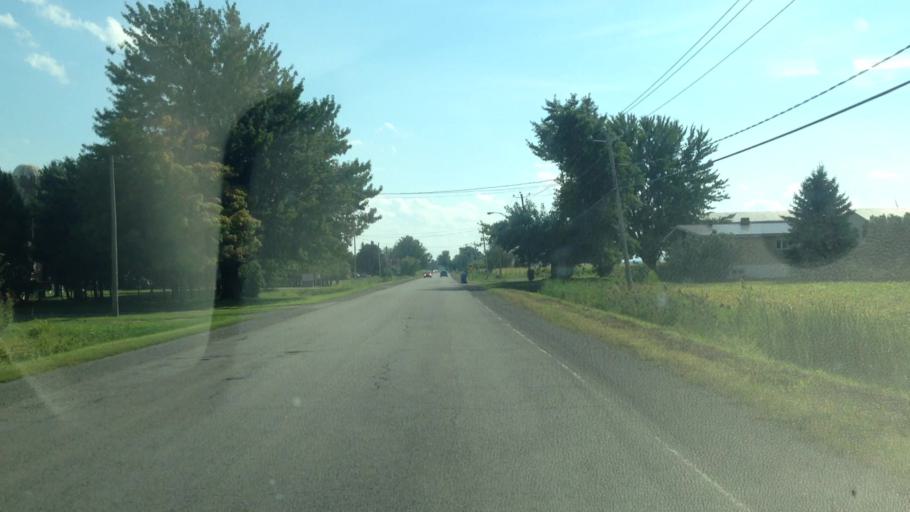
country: CA
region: Quebec
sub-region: Monteregie
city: Mercier
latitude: 45.2789
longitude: -73.6909
